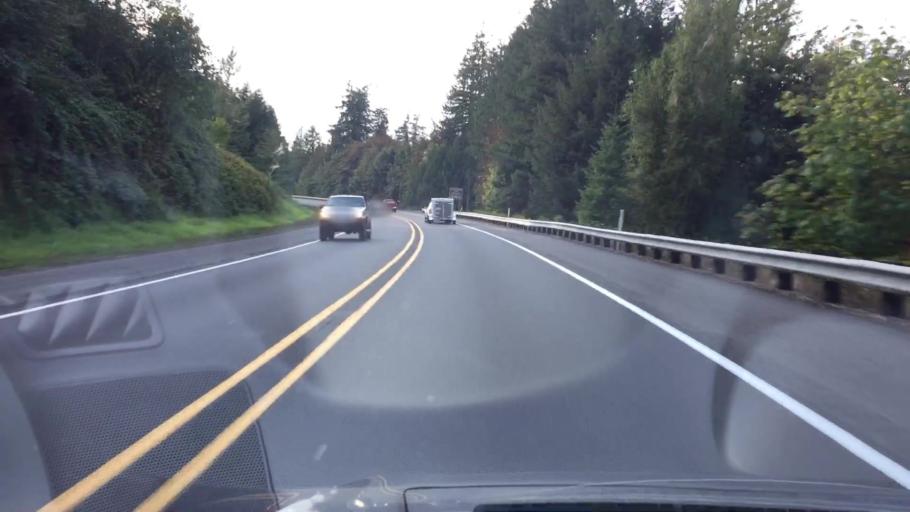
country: US
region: Washington
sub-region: Lewis County
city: Morton
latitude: 46.5349
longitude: -122.5405
